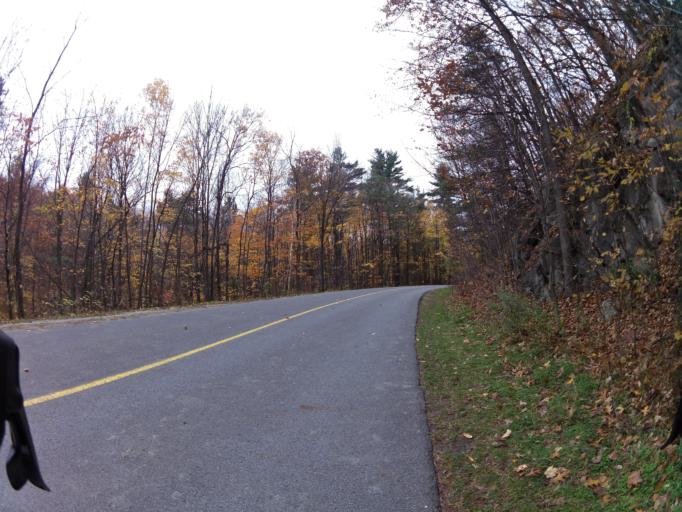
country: CA
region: Quebec
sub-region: Outaouais
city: Gatineau
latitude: 45.4677
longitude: -75.8131
